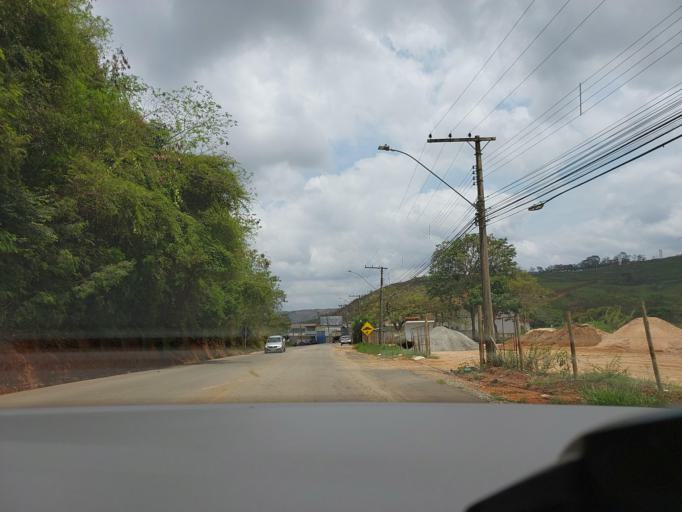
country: BR
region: Minas Gerais
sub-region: Ponte Nova
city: Ponte Nova
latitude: -20.3994
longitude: -42.8830
